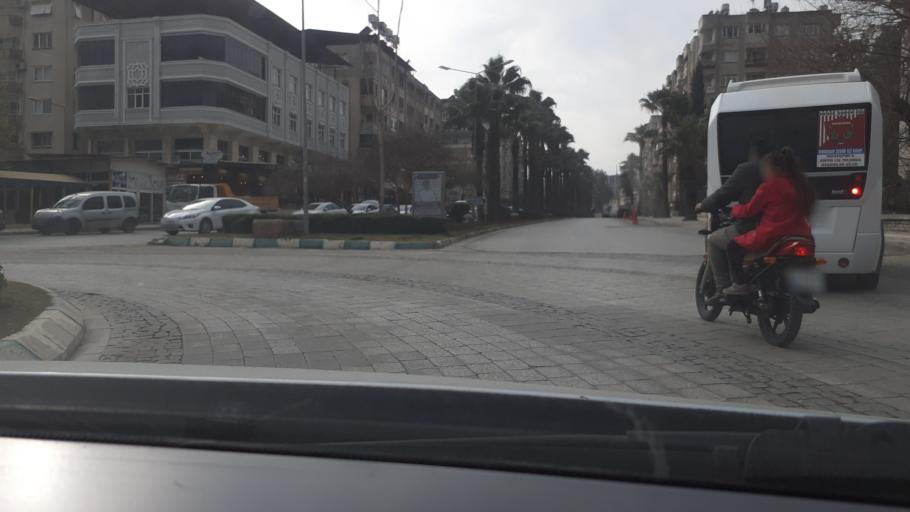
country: TR
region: Hatay
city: Kirikhan
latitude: 36.4988
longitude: 36.3510
